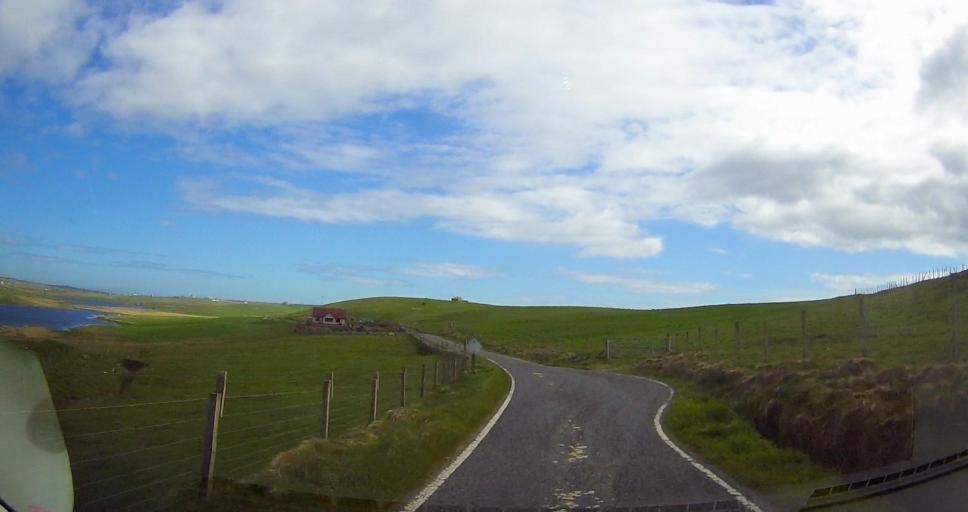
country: GB
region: Scotland
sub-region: Shetland Islands
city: Sandwick
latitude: 59.9267
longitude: -1.3449
